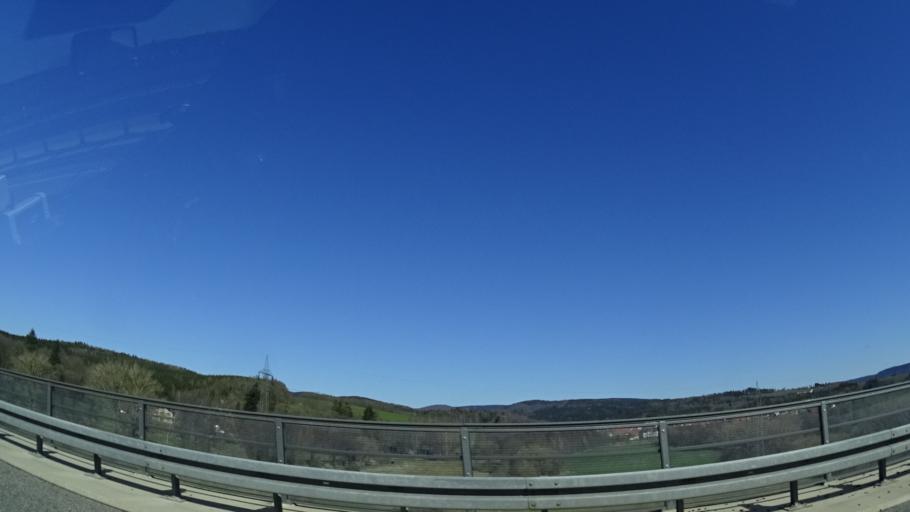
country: DE
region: Thuringia
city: Schleusingen
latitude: 50.5125
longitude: 10.7755
